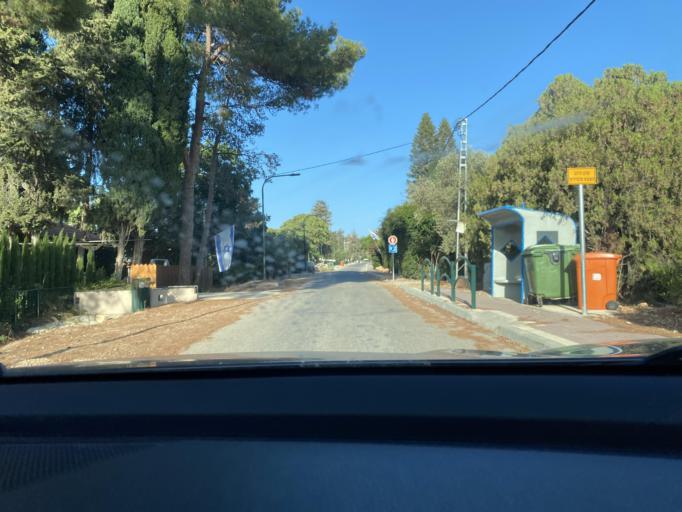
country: IL
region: Northern District
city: Shelomi
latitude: 33.0684
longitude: 35.1350
